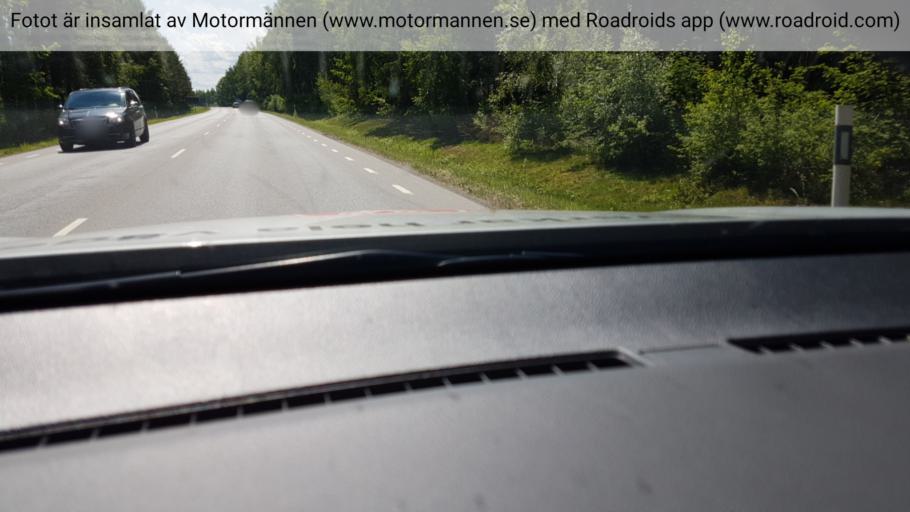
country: SE
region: Vaestra Goetaland
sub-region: Lidkopings Kommun
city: Lidkoping
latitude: 58.5164
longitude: 13.1157
